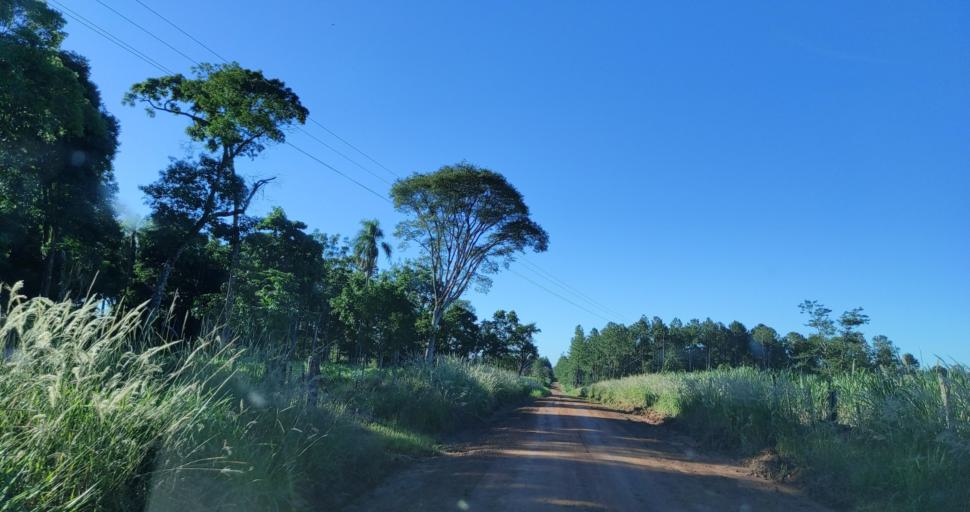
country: AR
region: Misiones
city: Garuhape
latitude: -26.8474
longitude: -55.0031
